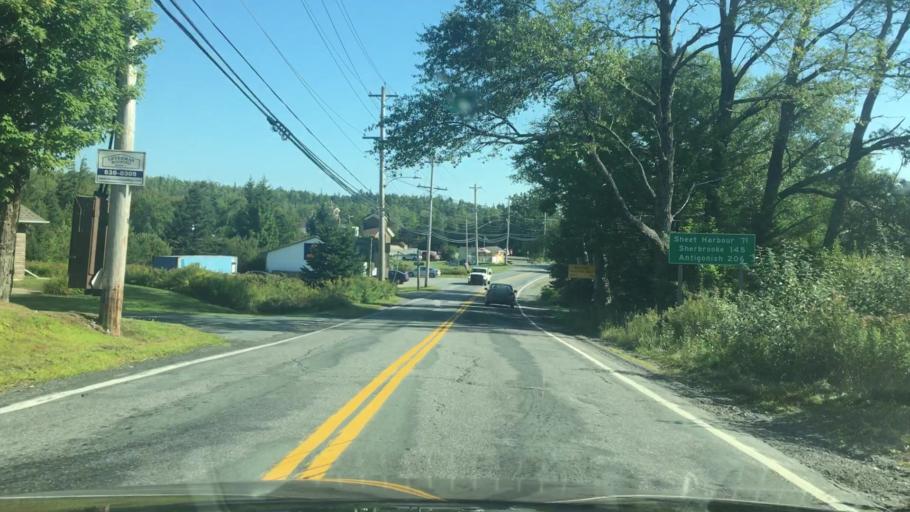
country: CA
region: Nova Scotia
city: Cole Harbour
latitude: 44.7873
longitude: -63.1480
